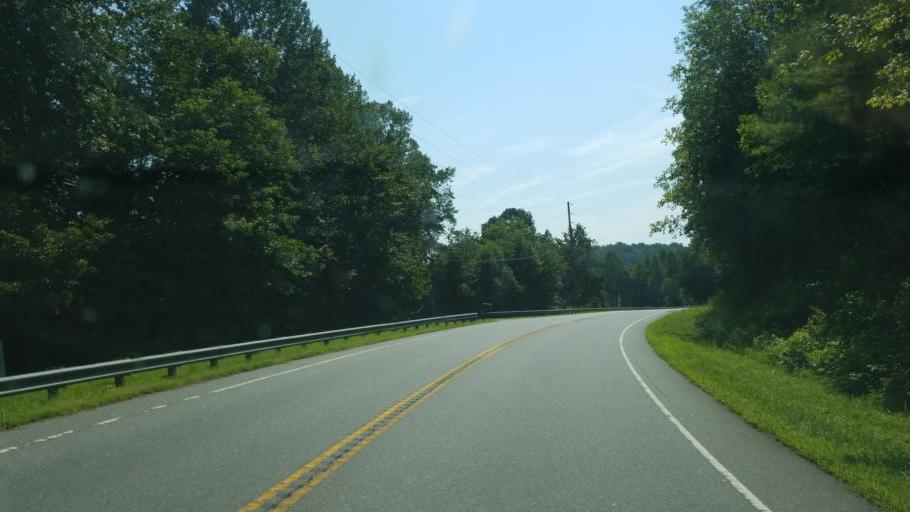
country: US
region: North Carolina
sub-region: Burke County
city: Glen Alpine
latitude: 35.8625
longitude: -81.7869
